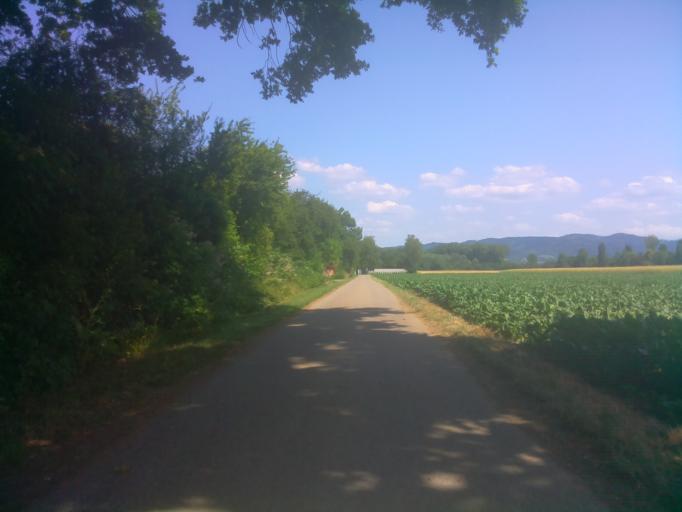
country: DE
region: Baden-Wuerttemberg
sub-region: Karlsruhe Region
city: Heddesheim
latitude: 49.5216
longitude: 8.6070
